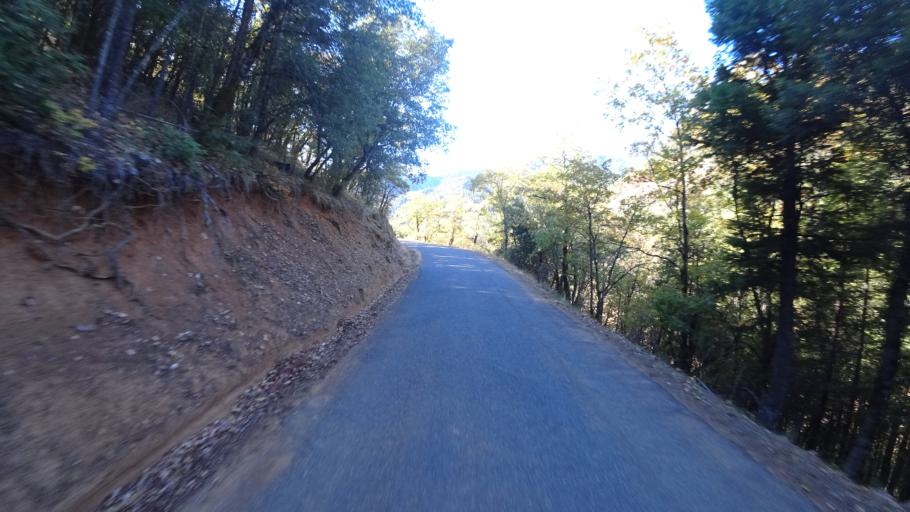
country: US
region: California
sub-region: Humboldt County
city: Willow Creek
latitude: 41.1813
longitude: -123.2184
